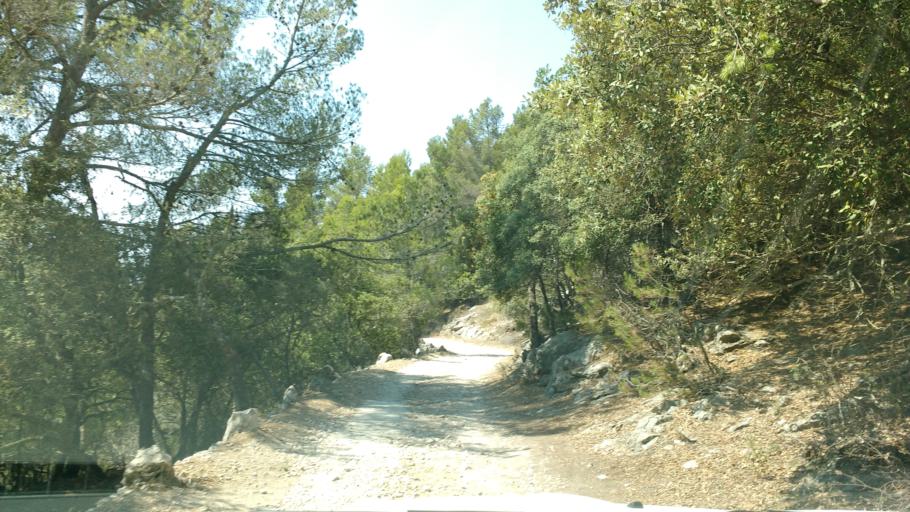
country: ES
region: Balearic Islands
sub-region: Illes Balears
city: Alaro
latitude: 39.7332
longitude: 2.7851
